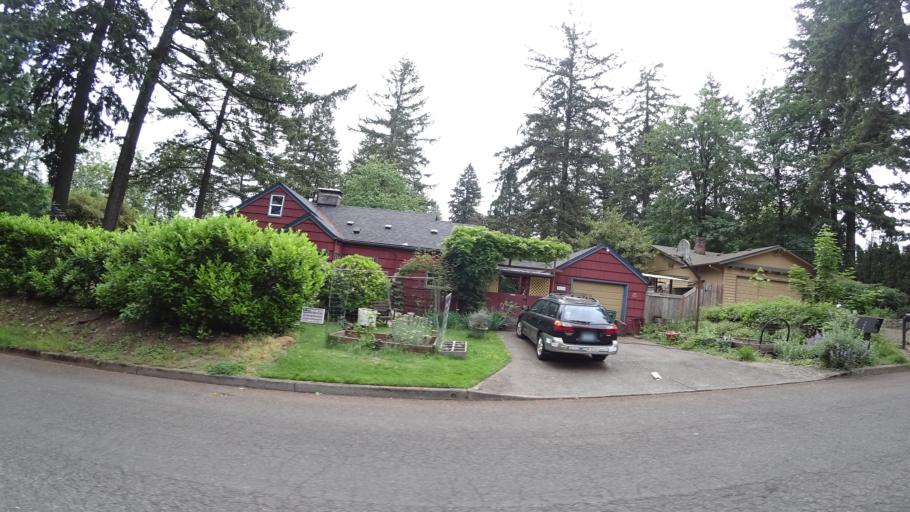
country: US
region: Oregon
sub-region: Washington County
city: Metzger
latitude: 45.4545
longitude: -122.7300
